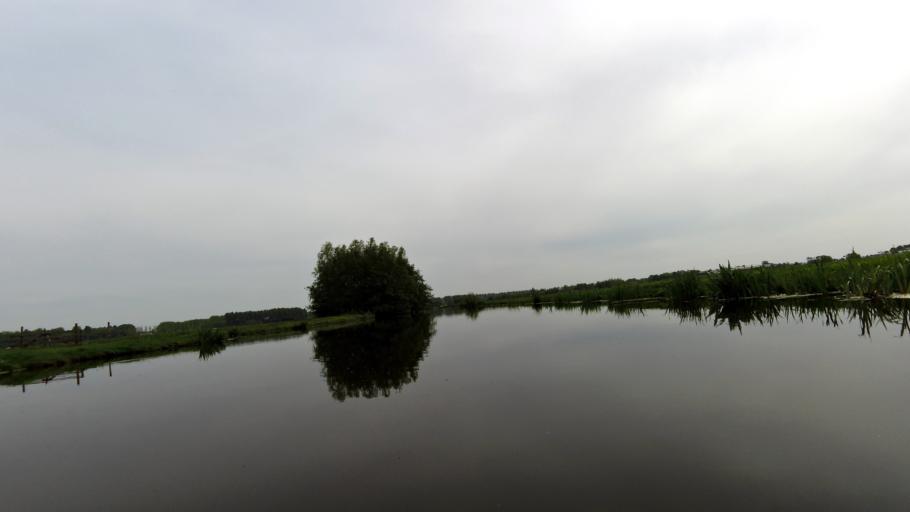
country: NL
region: South Holland
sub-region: Bodegraven-Reeuwijk
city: Reeuwijk
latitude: 52.0661
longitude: 4.7195
